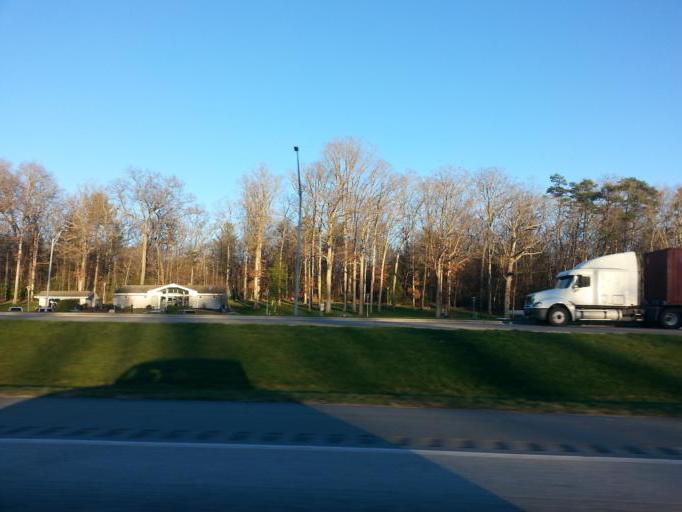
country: US
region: North Carolina
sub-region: Henderson County
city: Fletcher
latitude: 35.4266
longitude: -82.5288
